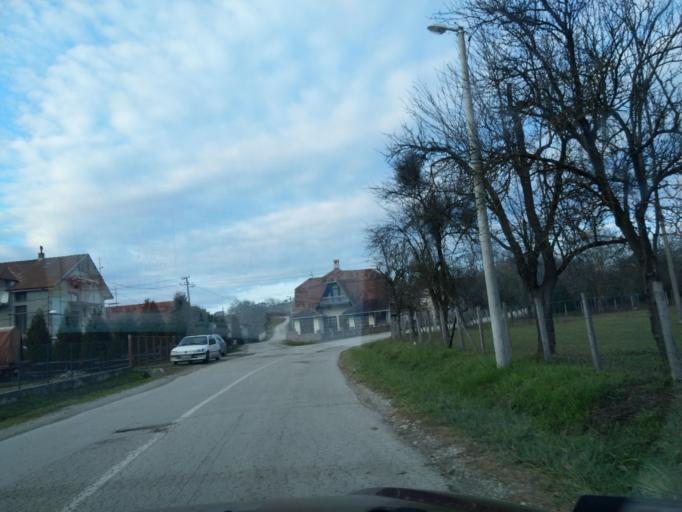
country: RS
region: Central Serbia
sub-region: Zlatiborski Okrug
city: Kosjeric
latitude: 43.9298
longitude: 19.8975
